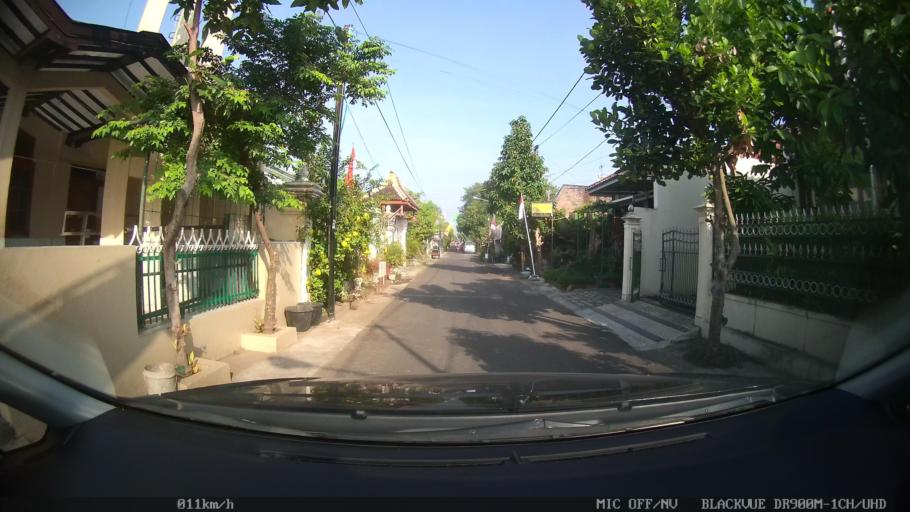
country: ID
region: Daerah Istimewa Yogyakarta
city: Yogyakarta
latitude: -7.8127
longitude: 110.3680
